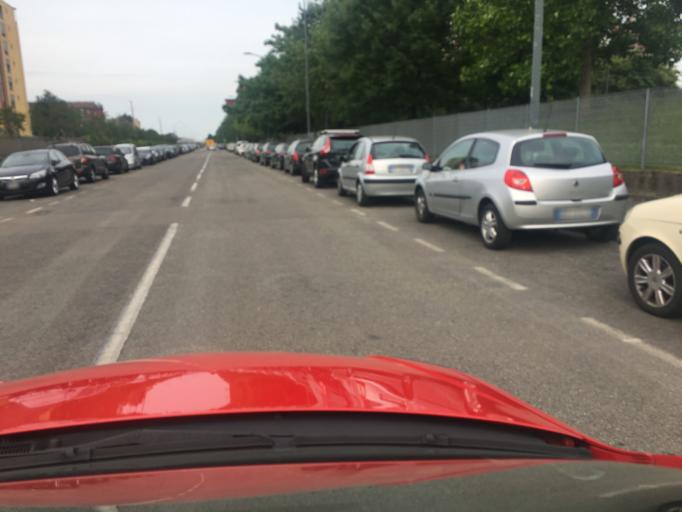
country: IT
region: Lombardy
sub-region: Citta metropolitana di Milano
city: Milano
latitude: 45.4458
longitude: 9.2156
